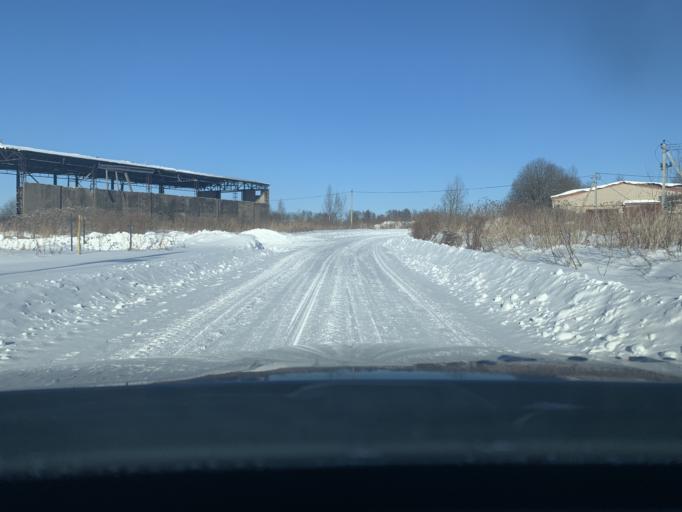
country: RU
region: Jaroslavl
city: Tunoshna
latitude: 57.6538
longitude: 40.0677
